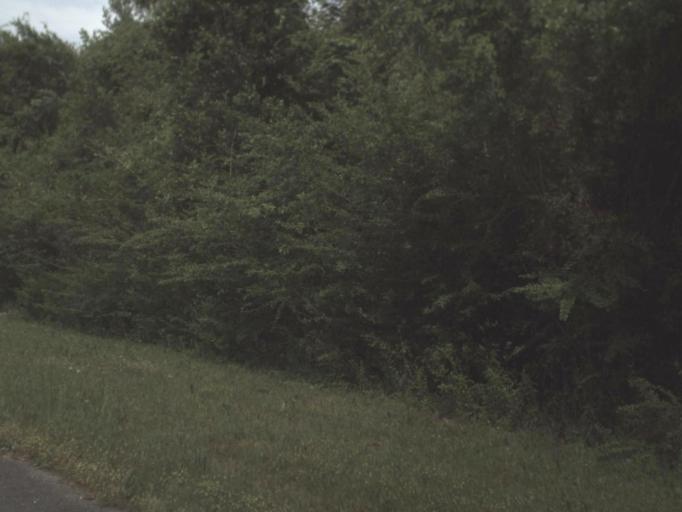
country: US
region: Alabama
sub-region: Escambia County
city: East Brewton
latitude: 30.9984
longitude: -87.1153
